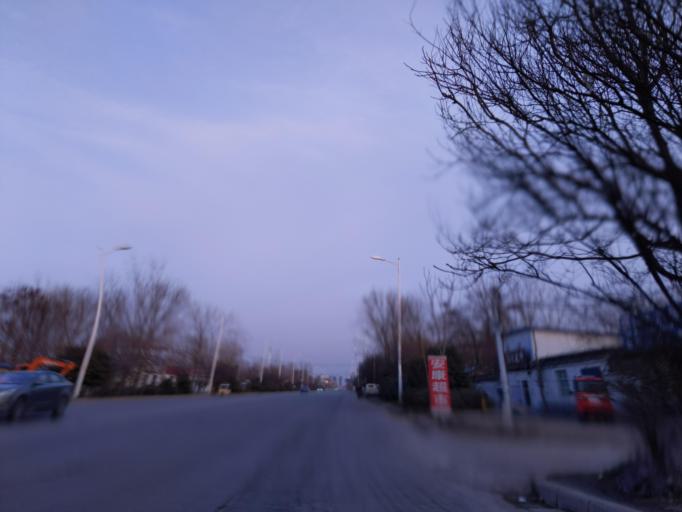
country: CN
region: Henan Sheng
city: Zhongyuanlu
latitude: 35.7871
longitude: 115.1221
